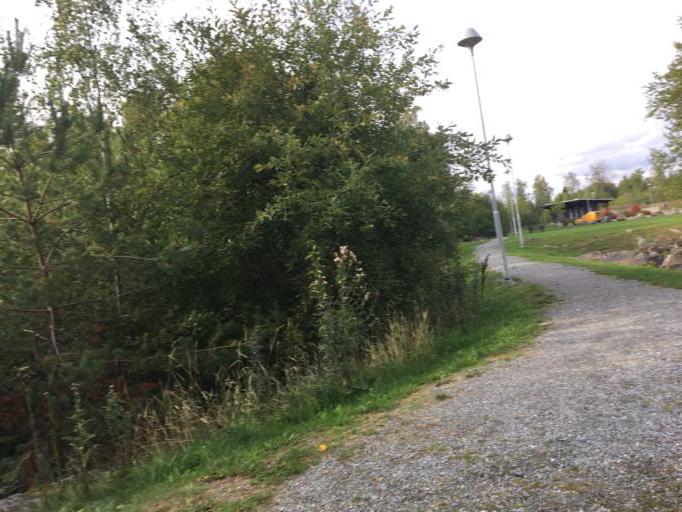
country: SE
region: Uppsala
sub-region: Enkopings Kommun
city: Hummelsta
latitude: 59.6373
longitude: 16.8749
